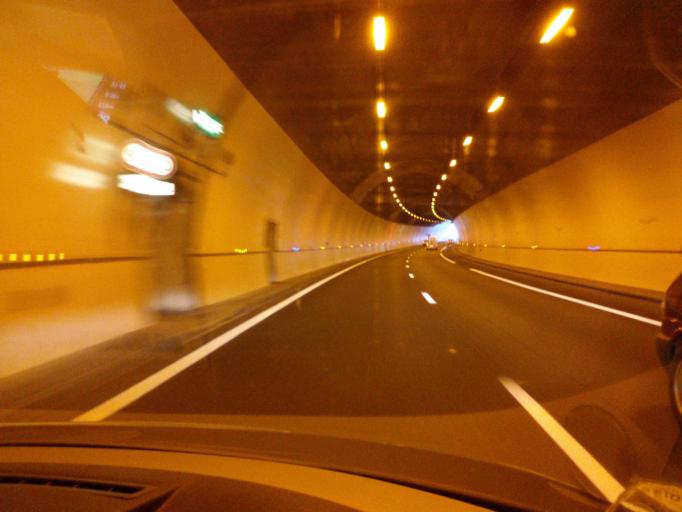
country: FR
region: Languedoc-Roussillon
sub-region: Departement de la Lozere
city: La Canourgue
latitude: 44.4823
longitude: 3.1989
